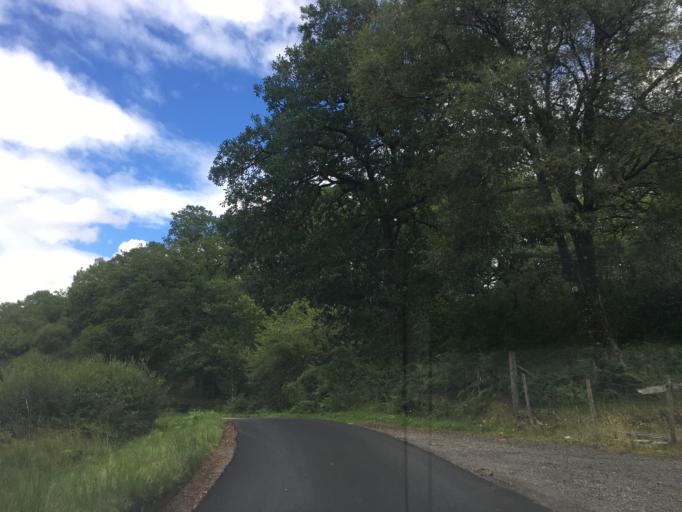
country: GB
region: Scotland
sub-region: Argyll and Bute
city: Oban
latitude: 56.3418
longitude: -5.1981
